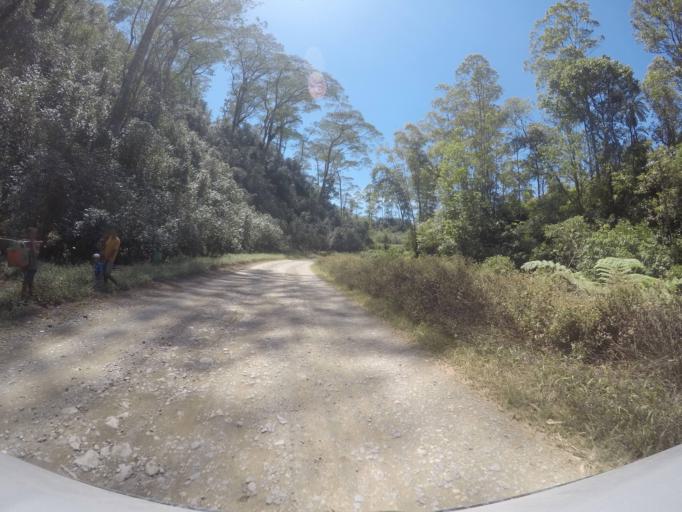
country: TL
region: Ermera
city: Gleno
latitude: -8.7753
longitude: 125.3883
